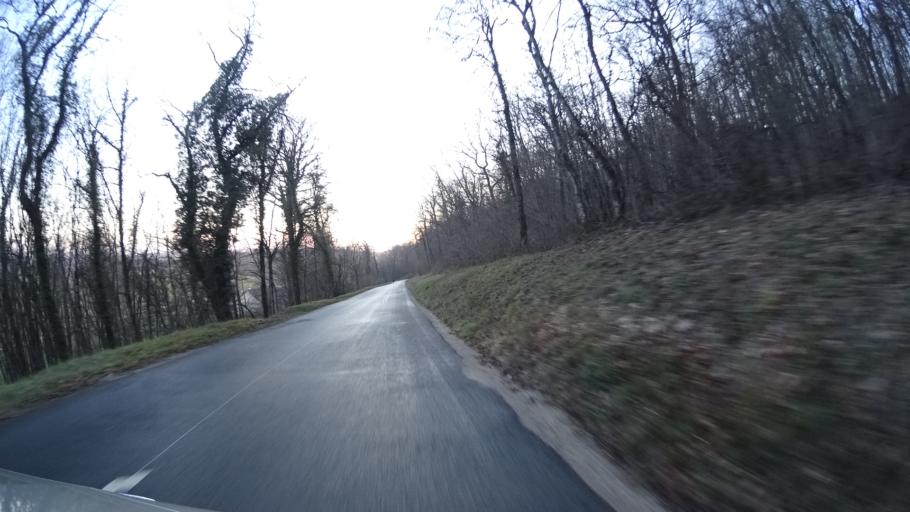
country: FR
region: Franche-Comte
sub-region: Departement du Doubs
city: Morre
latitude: 47.2111
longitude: 6.0547
